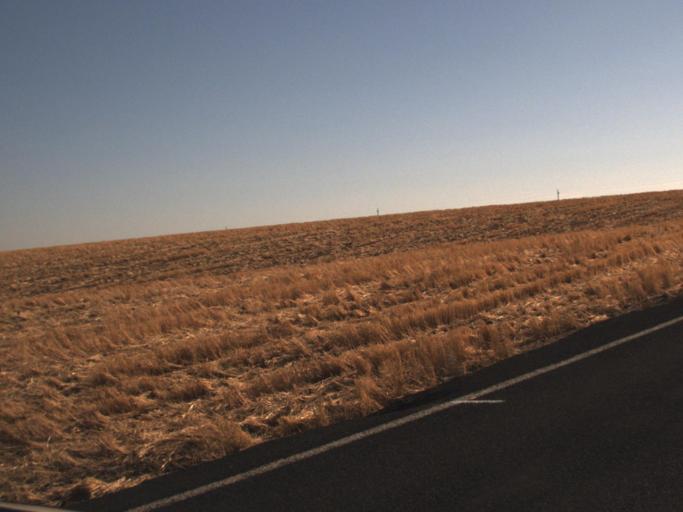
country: US
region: Washington
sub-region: Adams County
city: Ritzville
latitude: 47.0317
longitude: -118.6633
